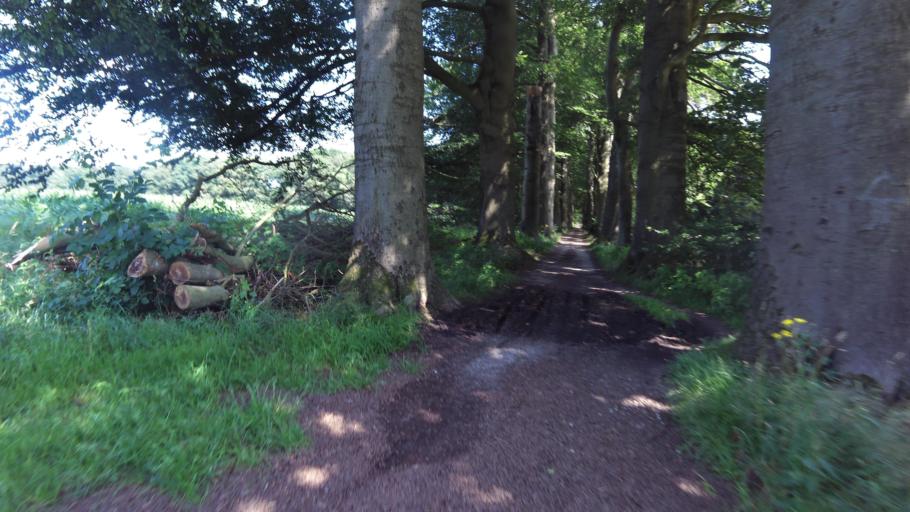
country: NL
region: Gelderland
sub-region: Gemeente Renkum
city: Oosterbeek
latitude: 51.9970
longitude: 5.8544
